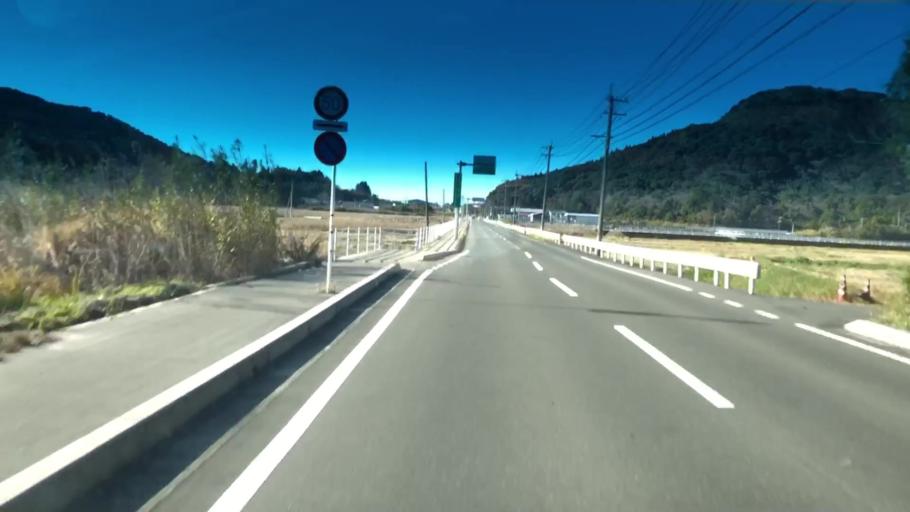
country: JP
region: Kagoshima
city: Satsumasendai
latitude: 31.8169
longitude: 130.2704
